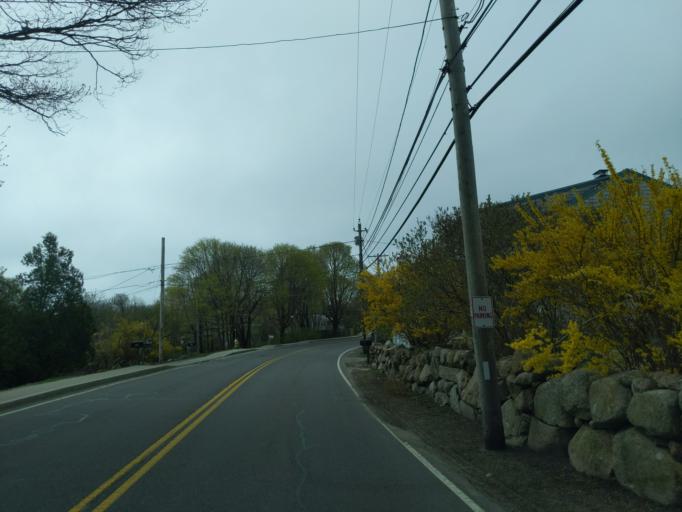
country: US
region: Massachusetts
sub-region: Essex County
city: Rockport
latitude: 42.6470
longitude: -70.5986
